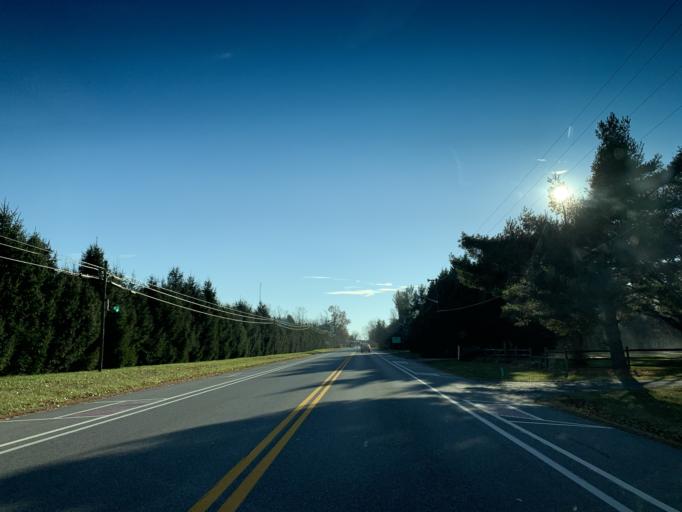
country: US
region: Delaware
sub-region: New Castle County
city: Middletown
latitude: 39.4101
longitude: -75.8647
